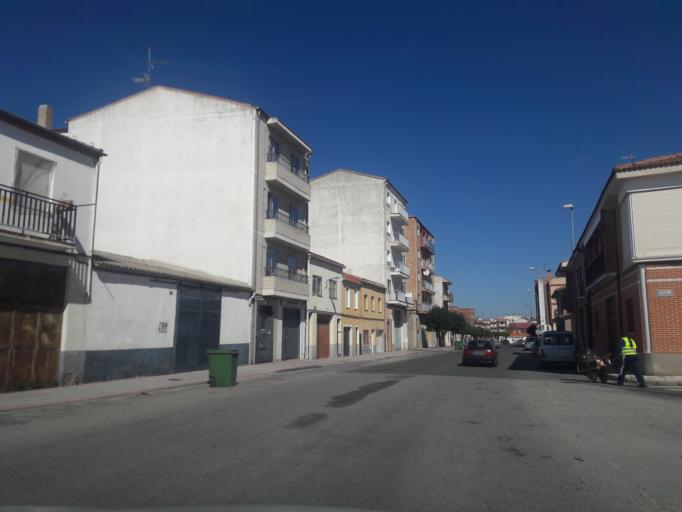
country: ES
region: Castille and Leon
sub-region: Provincia de Salamanca
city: Penaranda de Bracamonte
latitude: 40.8959
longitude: -5.2001
